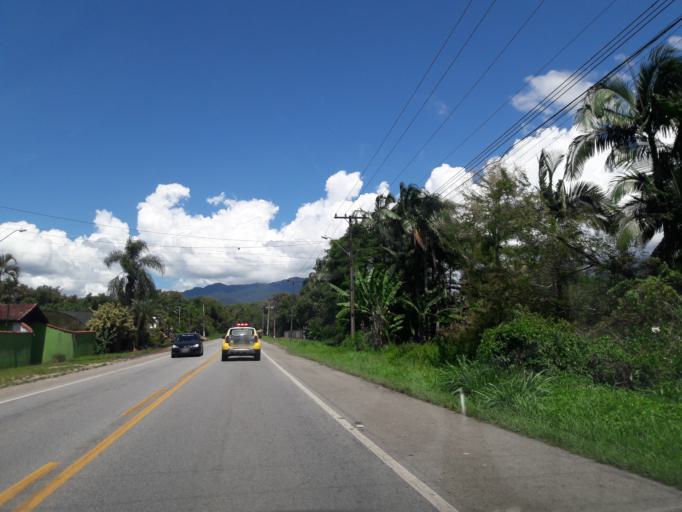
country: BR
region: Parana
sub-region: Antonina
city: Antonina
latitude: -25.5062
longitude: -48.8141
